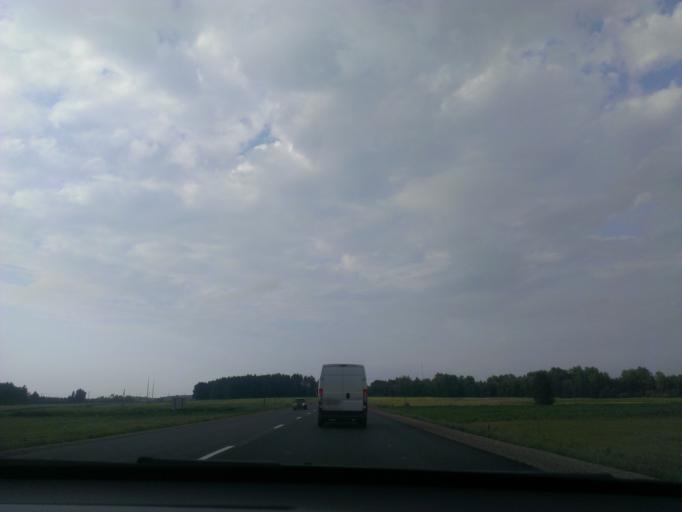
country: LV
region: Lecava
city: Iecava
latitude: 56.6469
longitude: 24.2283
